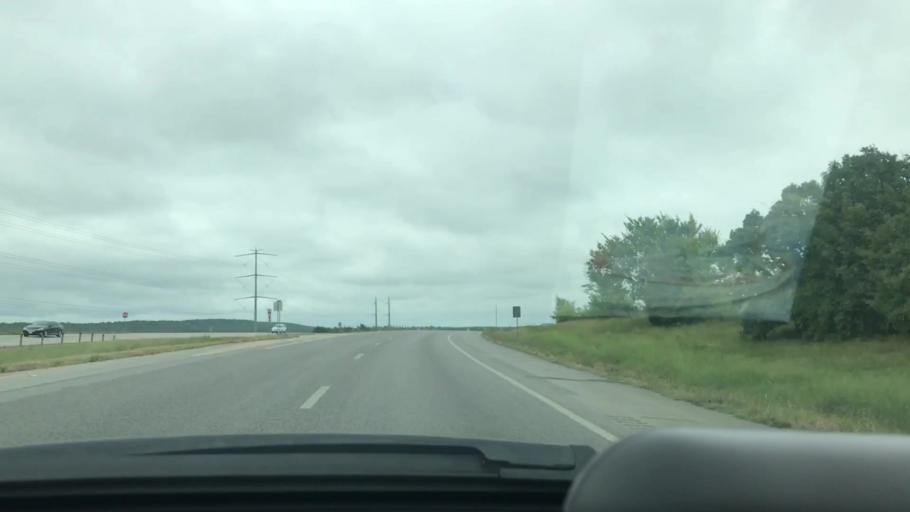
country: US
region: Oklahoma
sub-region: Pittsburg County
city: McAlester
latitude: 34.6762
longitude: -95.9342
